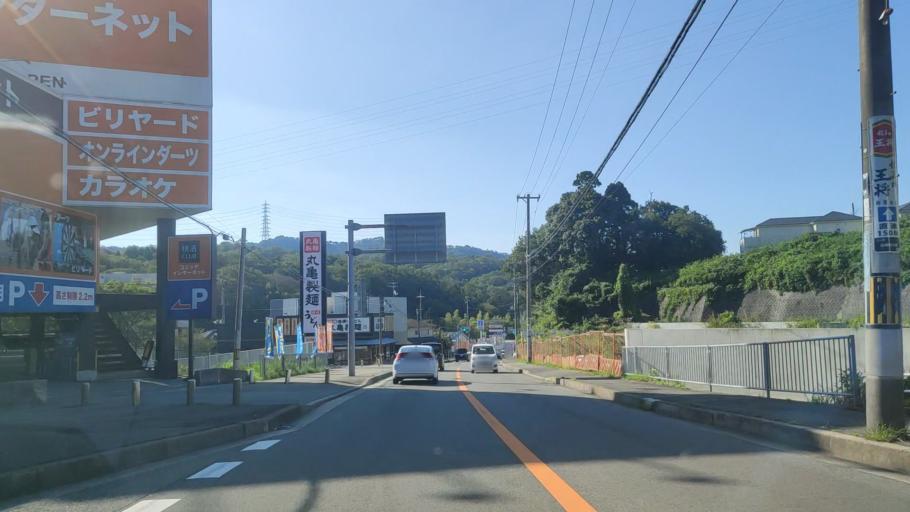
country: JP
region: Hyogo
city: Kobe
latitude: 34.7298
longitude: 135.1599
